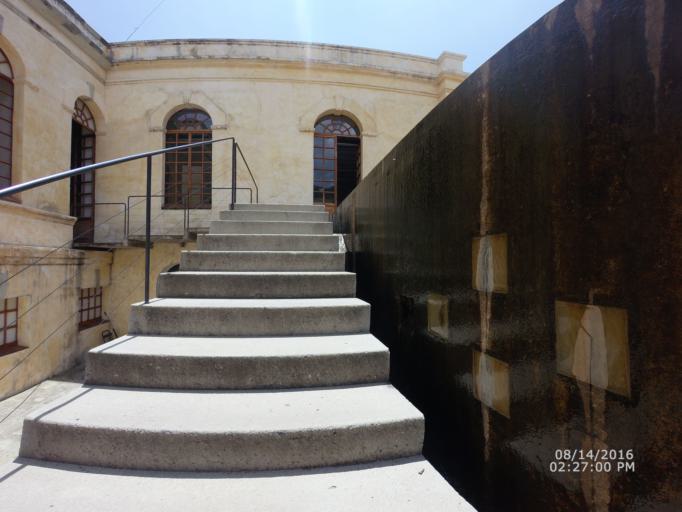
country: MX
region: Oaxaca
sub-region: San Juan Bautista Guelache
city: Fraccionamiento San Miguel
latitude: 17.1973
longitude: -96.7605
